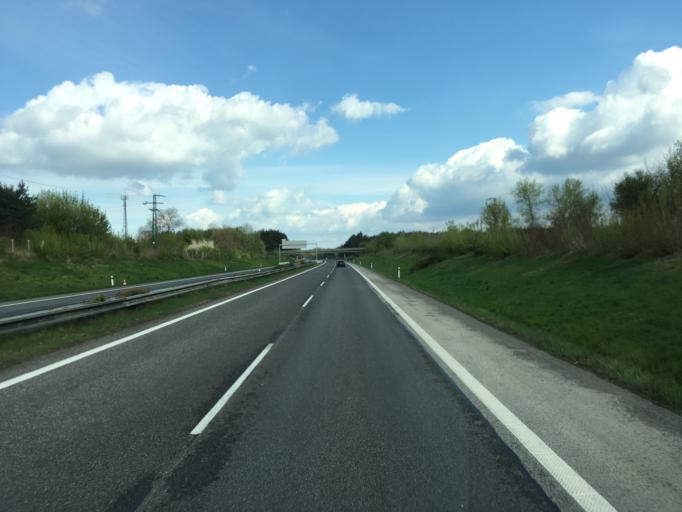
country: SK
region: Bratislavsky
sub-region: Okres Malacky
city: Malacky
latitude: 48.4391
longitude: 17.0431
